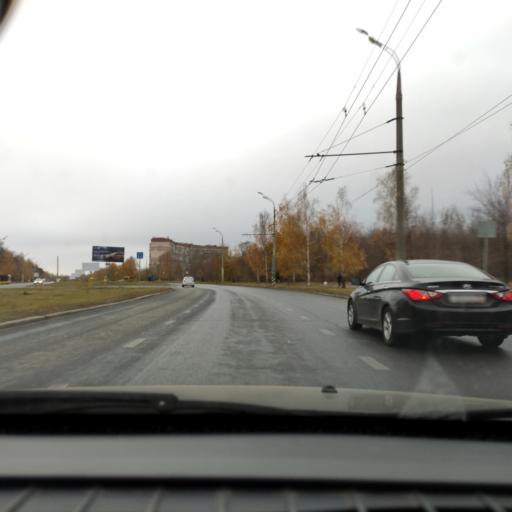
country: RU
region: Samara
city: Tol'yatti
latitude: 53.5052
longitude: 49.2552
